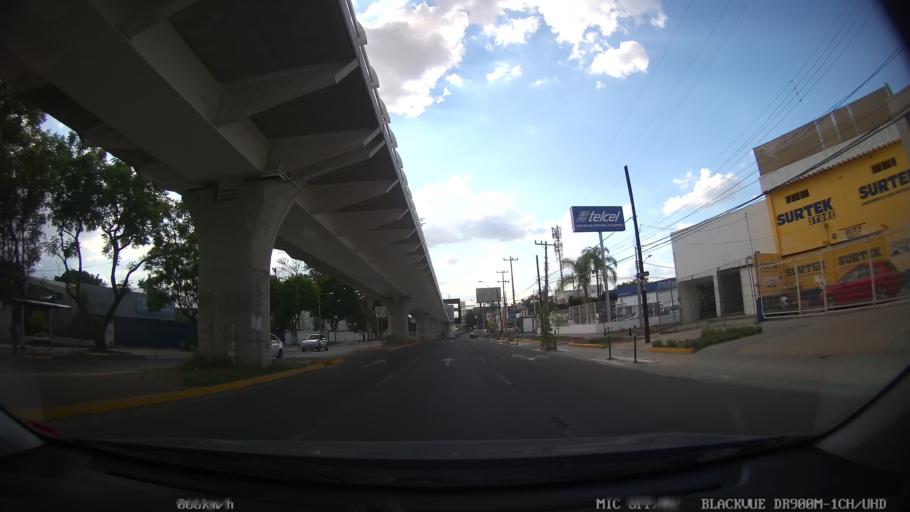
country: MX
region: Jalisco
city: Tlaquepaque
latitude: 20.6578
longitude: -103.3209
